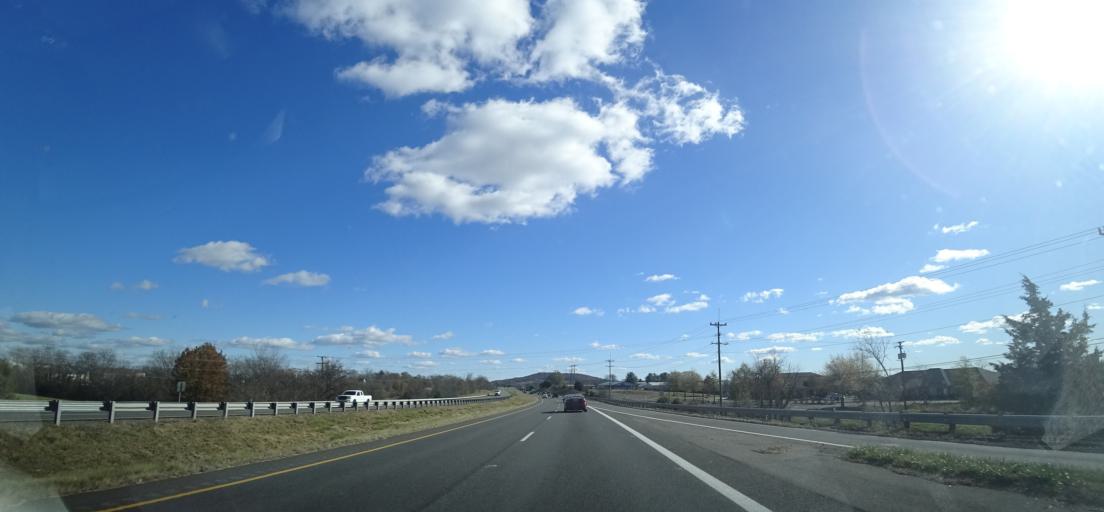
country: US
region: Virginia
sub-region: Culpeper County
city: Culpeper
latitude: 38.4453
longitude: -78.0061
